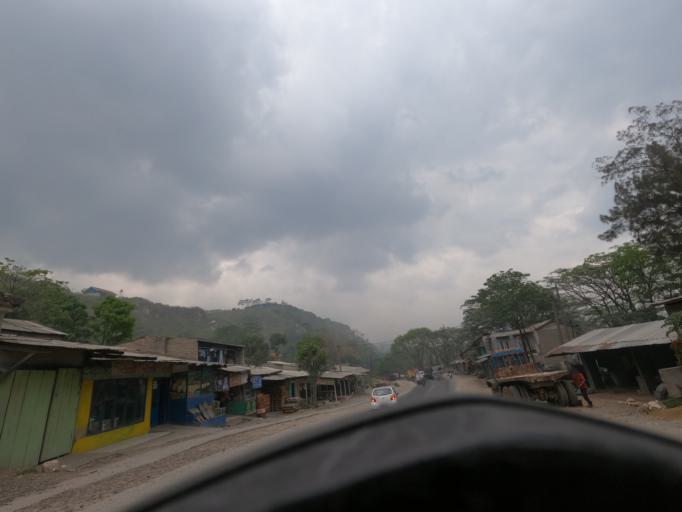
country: ID
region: West Java
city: Padalarang
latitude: -6.8319
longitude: 107.4486
